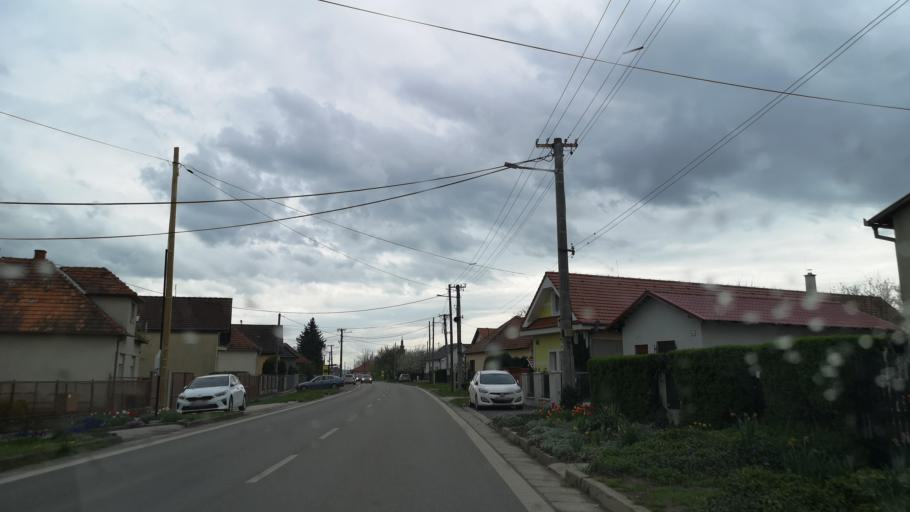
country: SK
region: Nitriansky
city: Zlate Moravce
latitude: 48.3444
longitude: 18.3611
